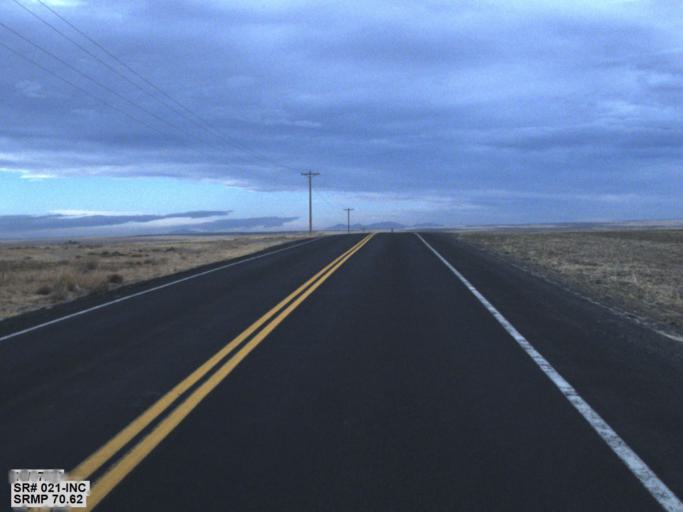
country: US
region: Washington
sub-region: Okanogan County
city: Coulee Dam
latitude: 47.5045
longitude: -118.7849
